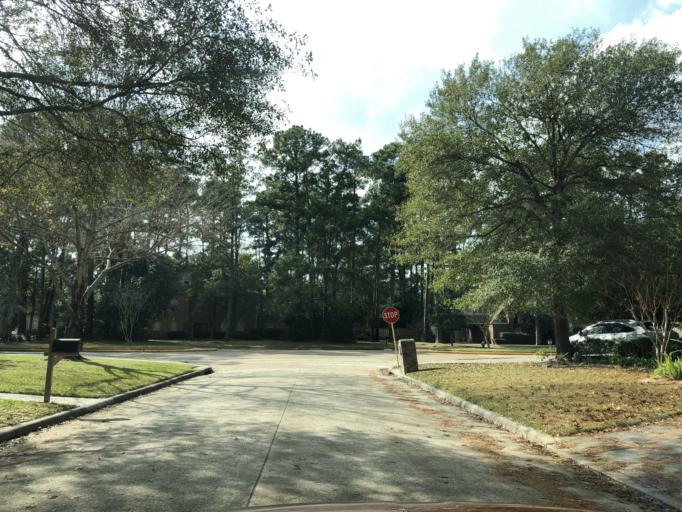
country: US
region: Texas
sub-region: Harris County
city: Tomball
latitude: 30.0231
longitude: -95.5476
